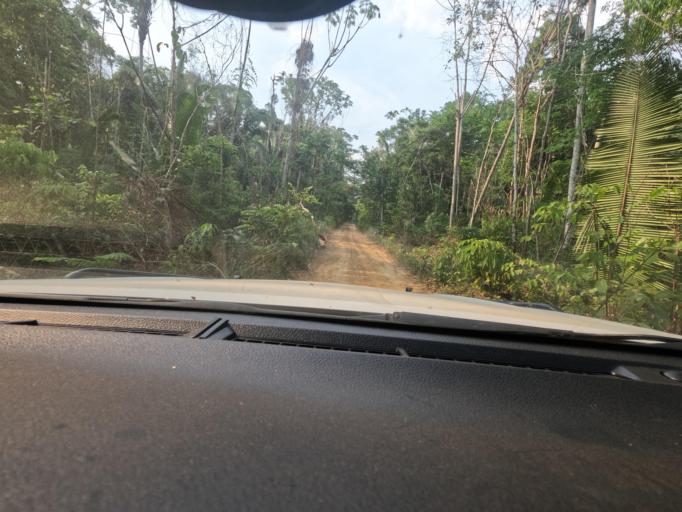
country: BR
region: Rondonia
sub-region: Porto Velho
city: Porto Velho
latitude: -8.6619
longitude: -63.1559
